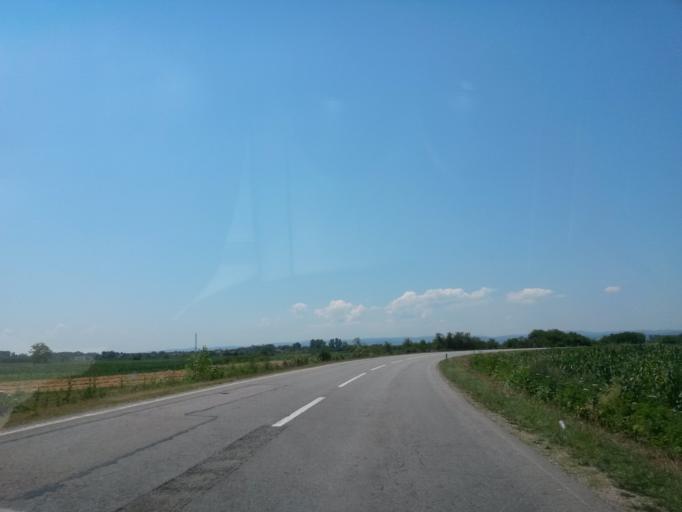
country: BA
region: Federation of Bosnia and Herzegovina
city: Donja Dubica
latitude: 45.0083
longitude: 18.3966
